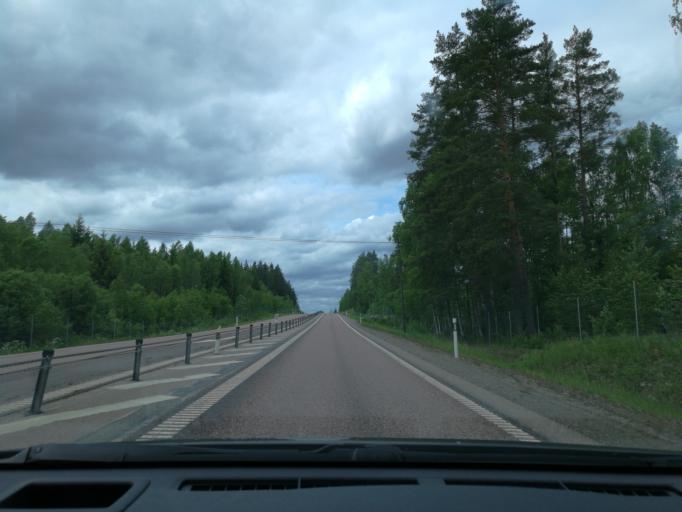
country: SE
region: Vaestmanland
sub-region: Fagersta Kommun
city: Fagersta
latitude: 59.9665
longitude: 15.8364
